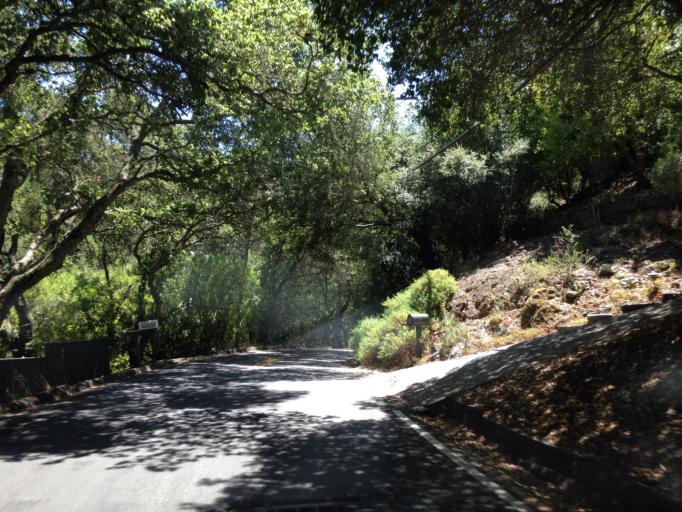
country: US
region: California
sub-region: Contra Costa County
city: Orinda
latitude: 37.8847
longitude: -122.2090
